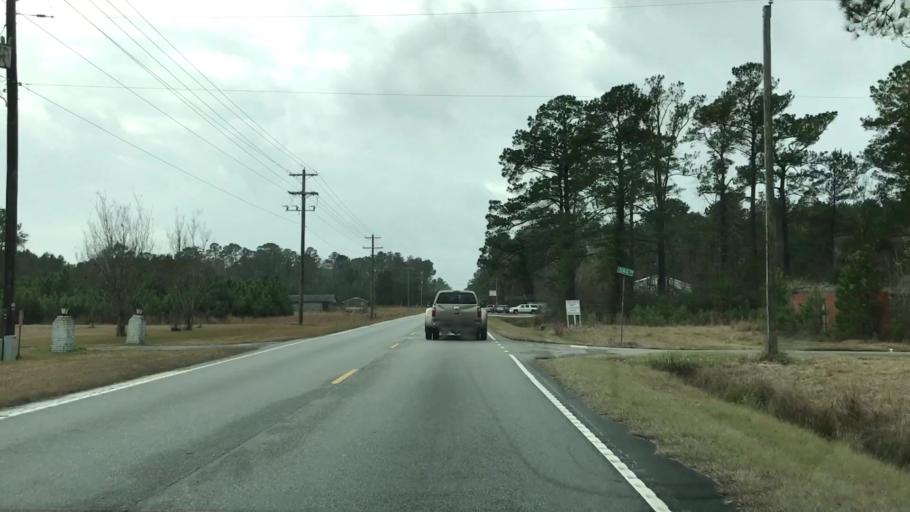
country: US
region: South Carolina
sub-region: Horry County
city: Socastee
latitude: 33.6955
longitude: -79.1135
